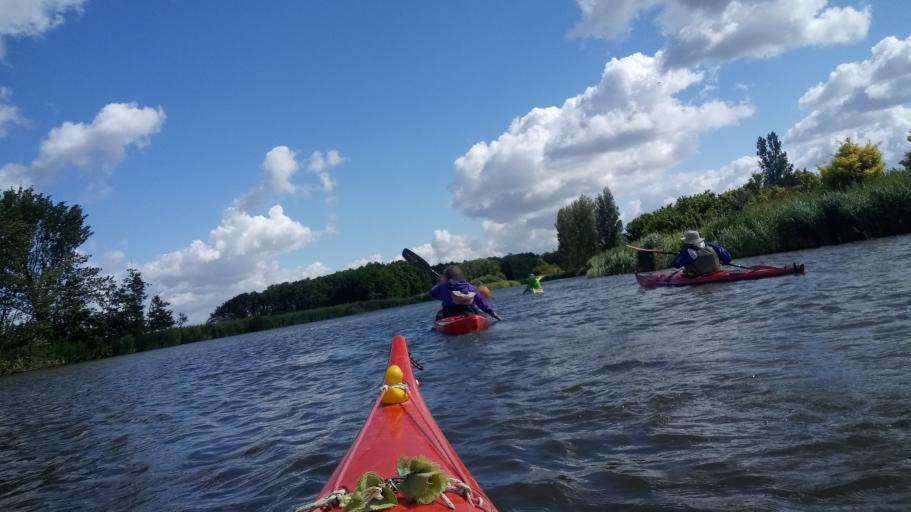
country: NL
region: North Holland
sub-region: Gemeente Enkhuizen
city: Enkhuizen
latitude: 52.7122
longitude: 5.1941
